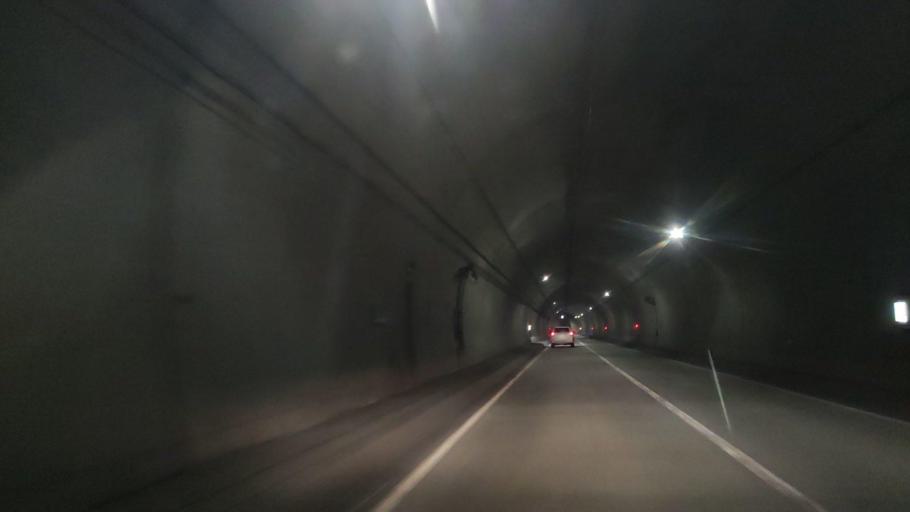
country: JP
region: Hokkaido
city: Rumoi
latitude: 43.7133
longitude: 141.3308
